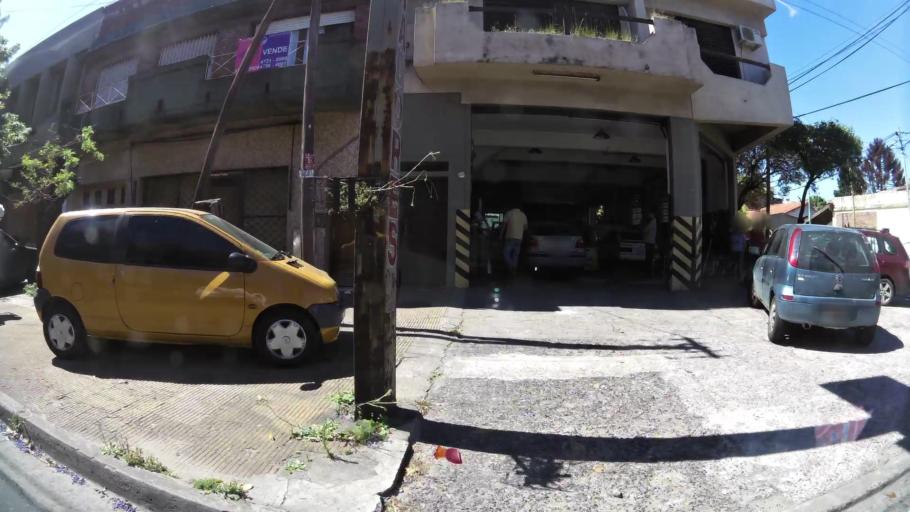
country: AR
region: Buenos Aires
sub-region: Partido de Vicente Lopez
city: Olivos
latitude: -34.5200
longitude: -58.5177
